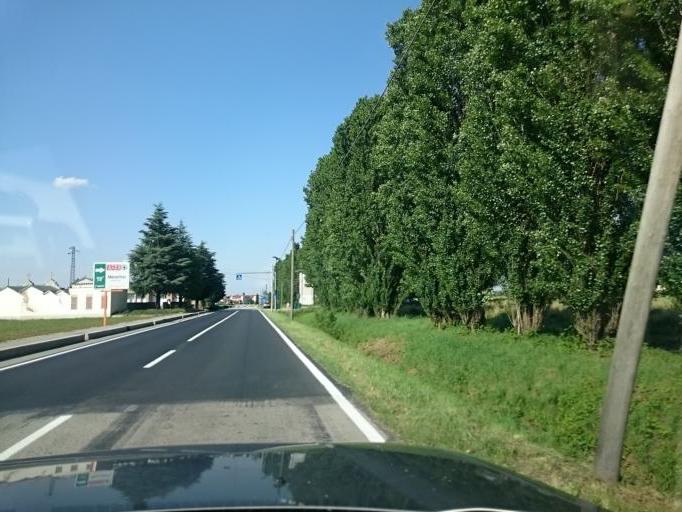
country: IT
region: Veneto
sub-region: Provincia di Padova
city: Arlesega
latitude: 45.4652
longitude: 11.6956
